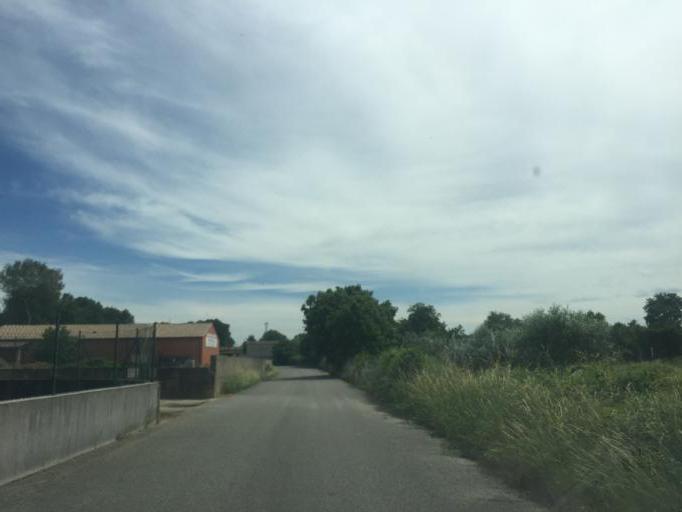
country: FR
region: Rhone-Alpes
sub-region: Departement de l'Ardeche
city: Bourg-Saint-Andeol
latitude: 44.3634
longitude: 4.6462
